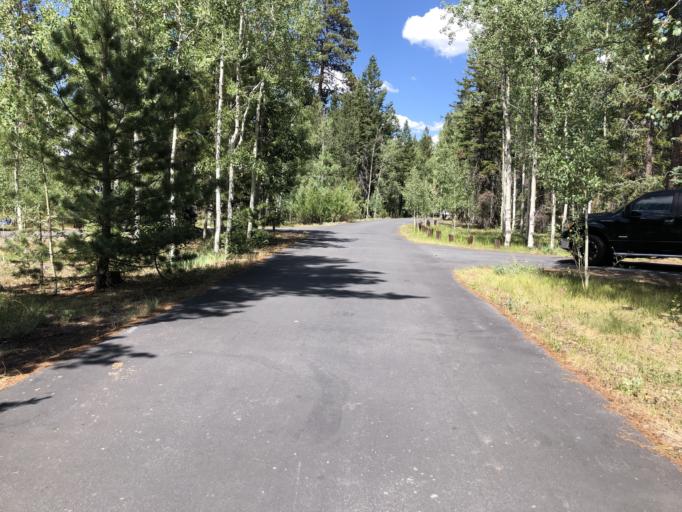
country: US
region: Arizona
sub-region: Apache County
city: Eagar
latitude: 33.8772
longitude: -109.4011
